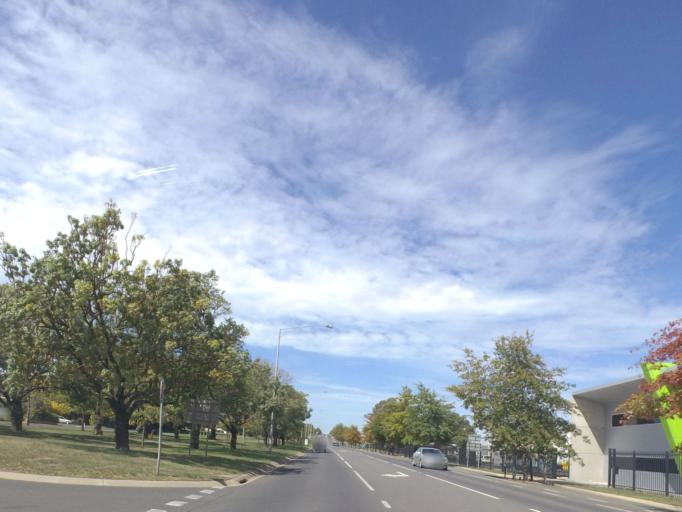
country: AU
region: Victoria
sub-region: Mount Alexander
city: Castlemaine
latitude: -37.2549
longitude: 144.4647
